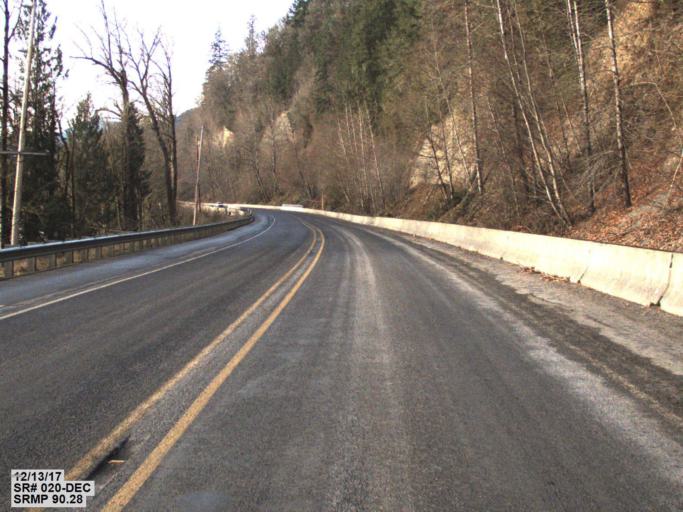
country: US
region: Washington
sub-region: Snohomish County
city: Darrington
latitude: 48.5325
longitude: -121.7235
